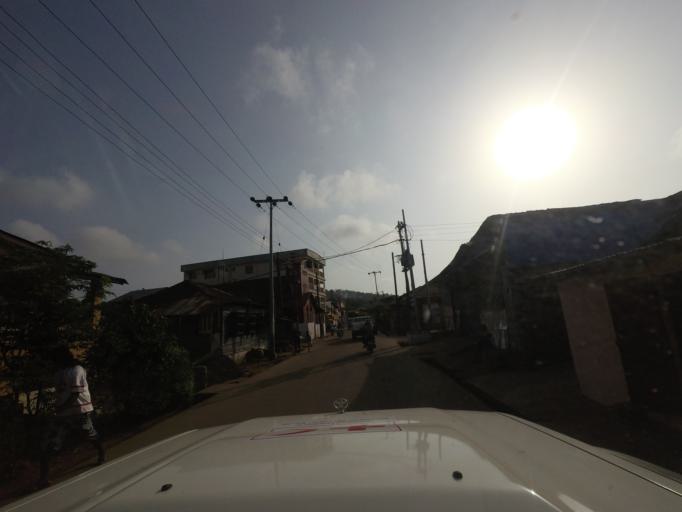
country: SL
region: Western Area
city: Freetown
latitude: 8.4838
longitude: -13.2528
